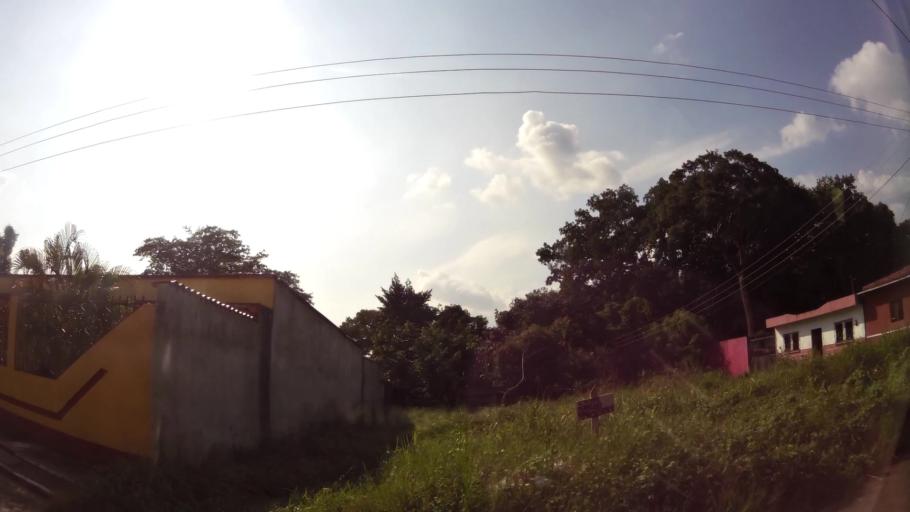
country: GT
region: Retalhuleu
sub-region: Municipio de Retalhuleu
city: Retalhuleu
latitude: 14.5392
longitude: -91.6939
